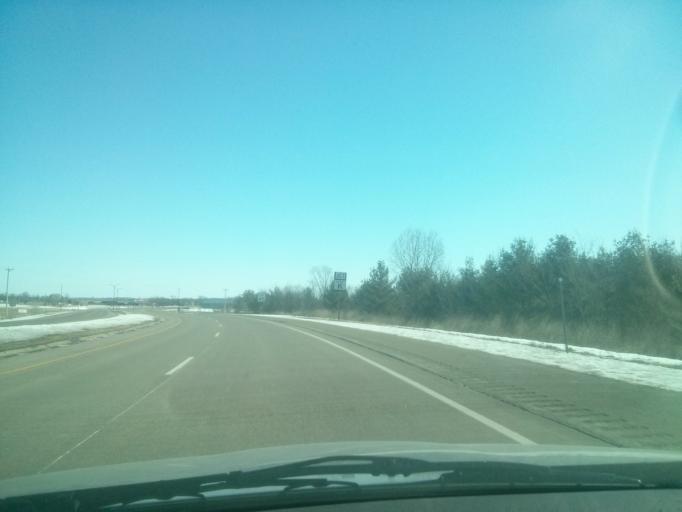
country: US
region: Wisconsin
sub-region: Saint Croix County
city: New Richmond
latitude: 45.1287
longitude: -92.5599
